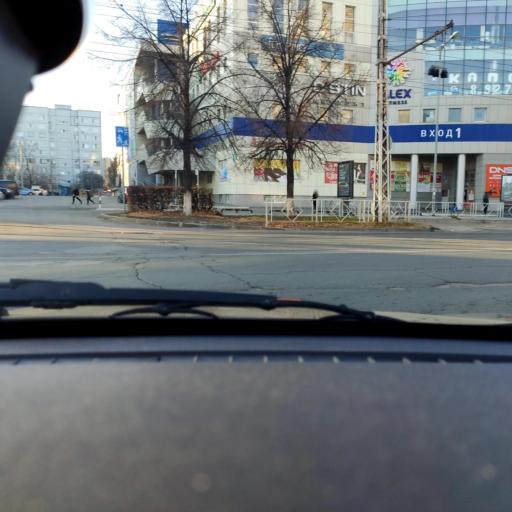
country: RU
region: Samara
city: Tol'yatti
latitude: 53.5345
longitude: 49.3207
